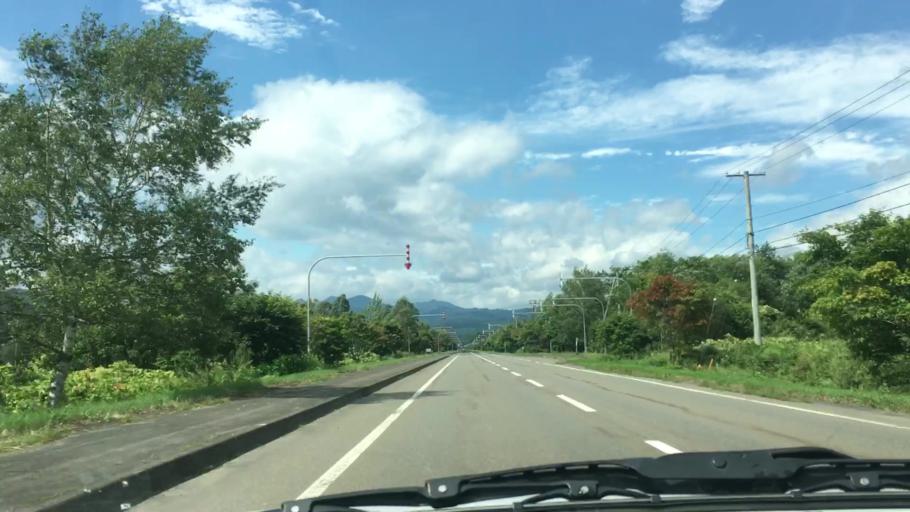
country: JP
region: Hokkaido
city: Otofuke
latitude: 43.3080
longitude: 143.3098
